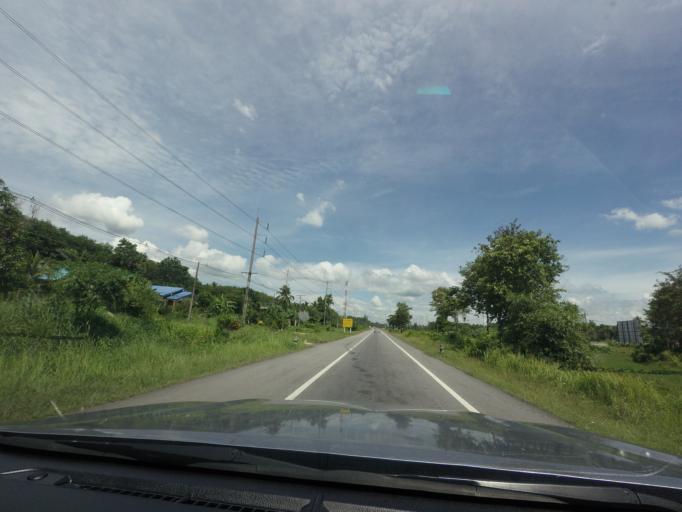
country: TH
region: Songkhla
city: Chana
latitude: 6.9821
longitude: 100.6809
